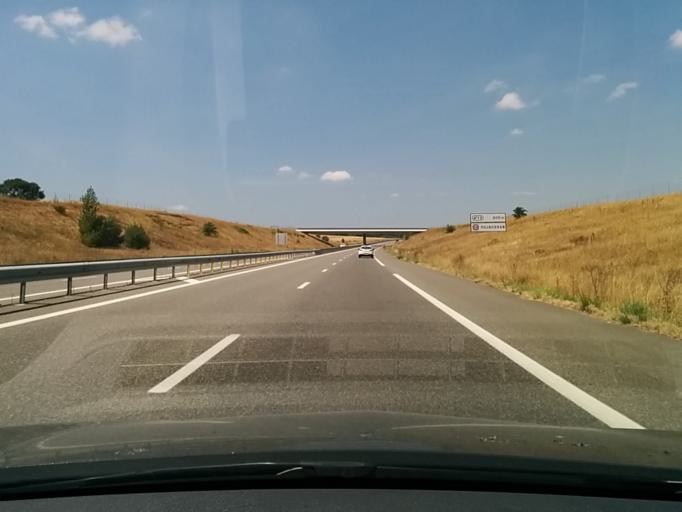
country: FR
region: Midi-Pyrenees
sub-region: Departement de la Haute-Garonne
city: Fontenilles
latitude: 43.5834
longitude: 1.1828
